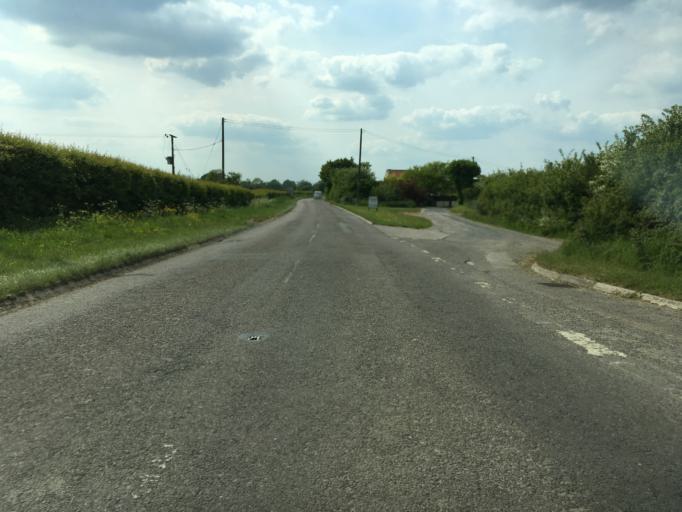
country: GB
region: England
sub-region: South Gloucestershire
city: Thornbury
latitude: 51.6276
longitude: -2.5398
